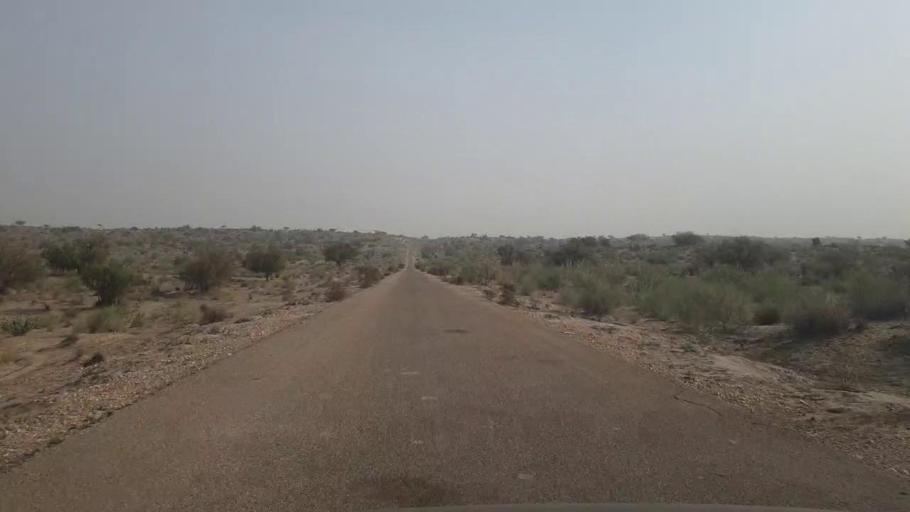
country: PK
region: Sindh
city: Chor
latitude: 25.4899
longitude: 69.9720
